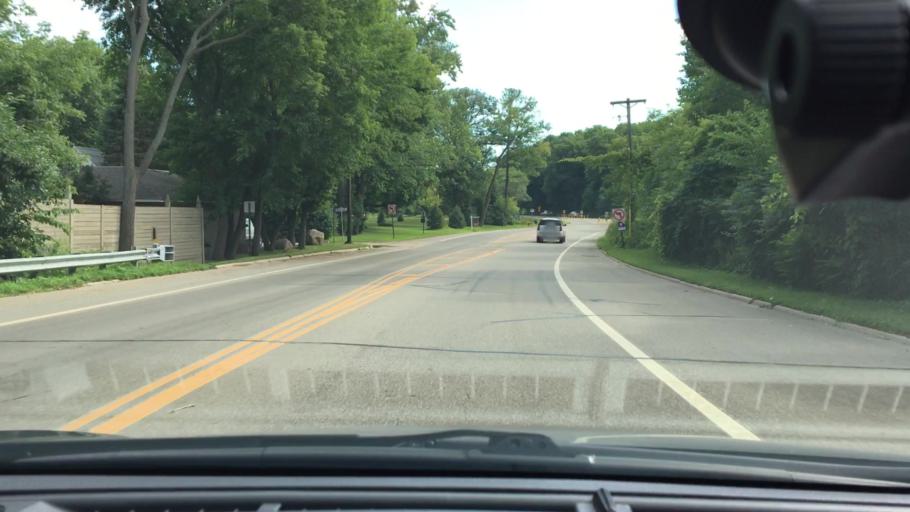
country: US
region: Minnesota
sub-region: Hennepin County
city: Tonka Bay
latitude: 44.9429
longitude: -93.5805
